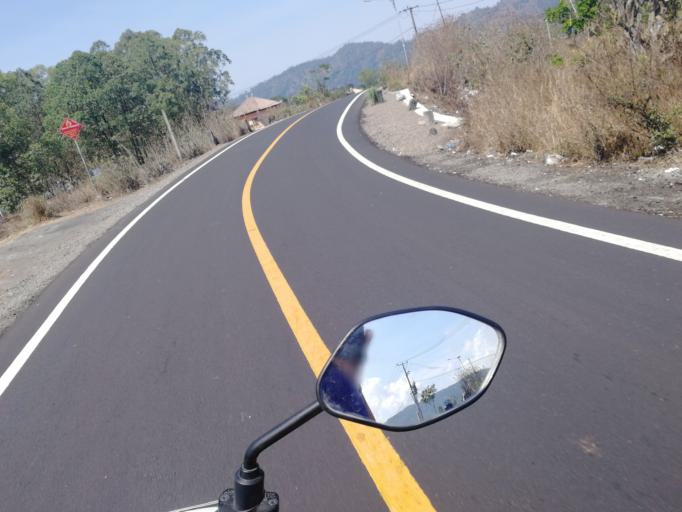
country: ID
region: Bali
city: Banjar Trunyan
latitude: -8.2537
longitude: 115.3965
